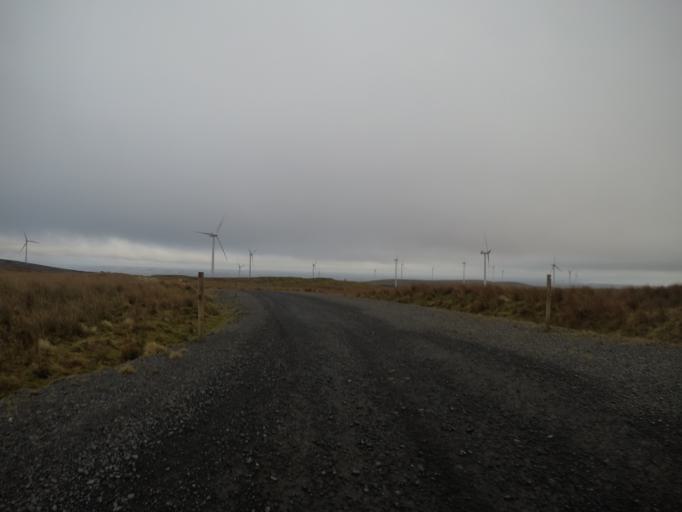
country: GB
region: Scotland
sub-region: North Ayrshire
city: Fairlie
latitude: 55.7436
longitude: -4.7958
